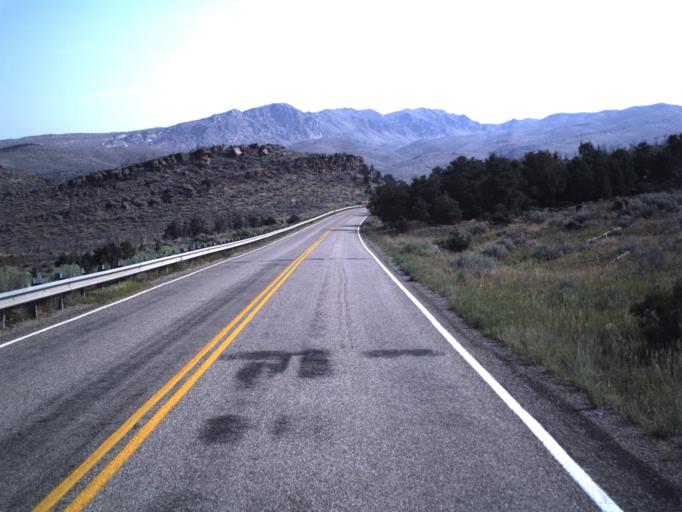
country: US
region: Utah
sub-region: Daggett County
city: Manila
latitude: 40.9250
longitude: -109.4167
